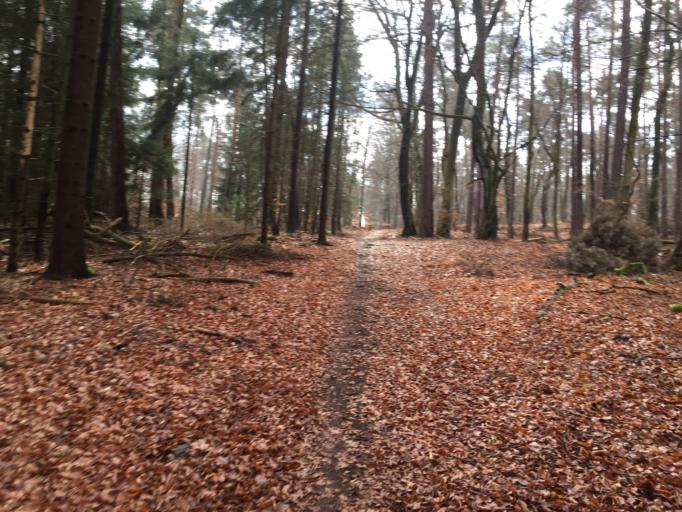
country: DE
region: Rheinland-Pfalz
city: Frankenstein
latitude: 49.4090
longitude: 7.9533
